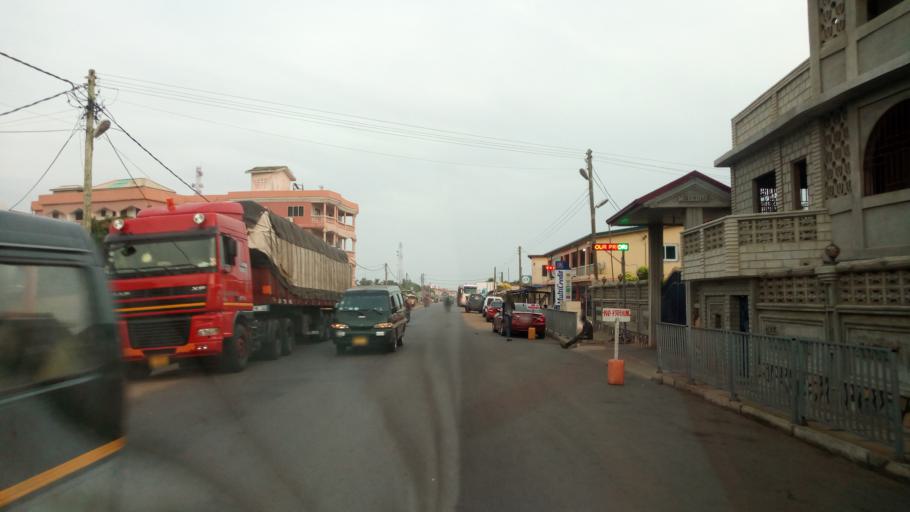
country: TG
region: Maritime
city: Lome
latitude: 6.1144
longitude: 1.1940
